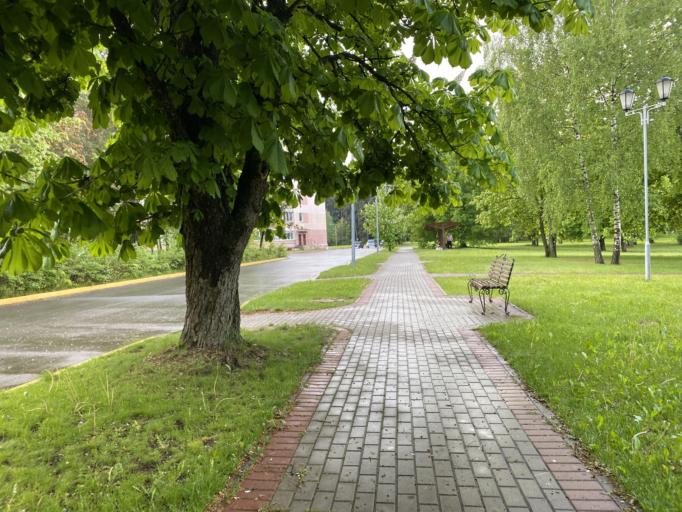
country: BY
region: Minsk
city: Lyasny
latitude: 54.0038
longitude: 27.6863
